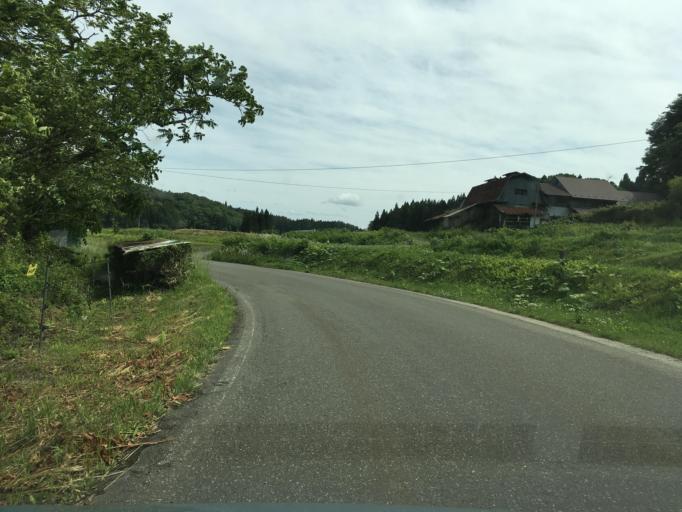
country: JP
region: Iwate
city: Mizusawa
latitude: 39.0840
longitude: 141.3520
